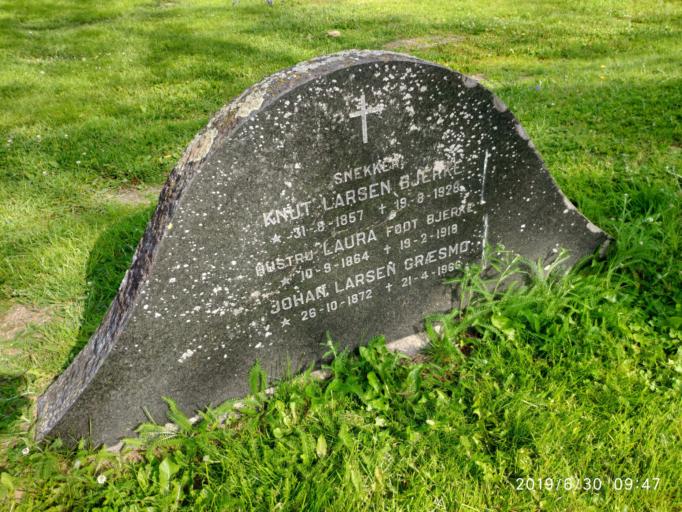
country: NO
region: Akershus
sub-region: Nannestad
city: Teigebyen
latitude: 60.2140
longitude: 11.0045
